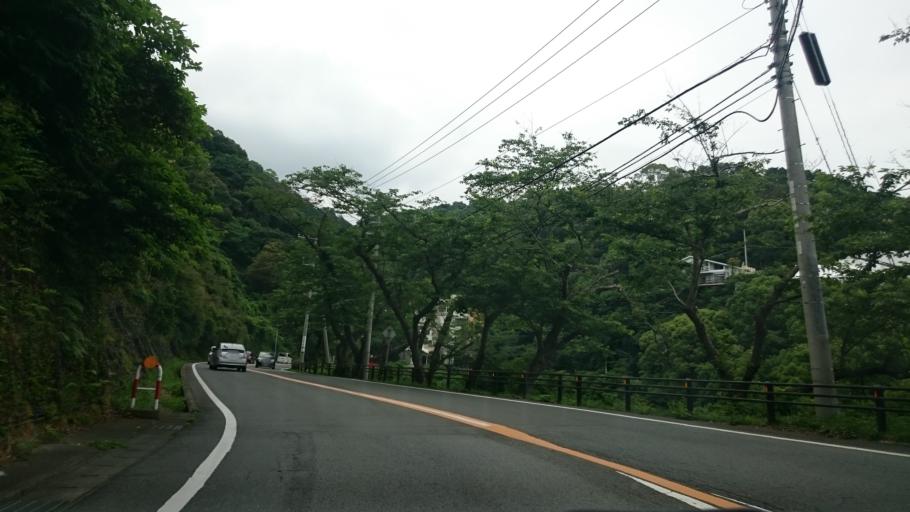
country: JP
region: Shizuoka
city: Ito
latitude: 35.0299
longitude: 139.0970
